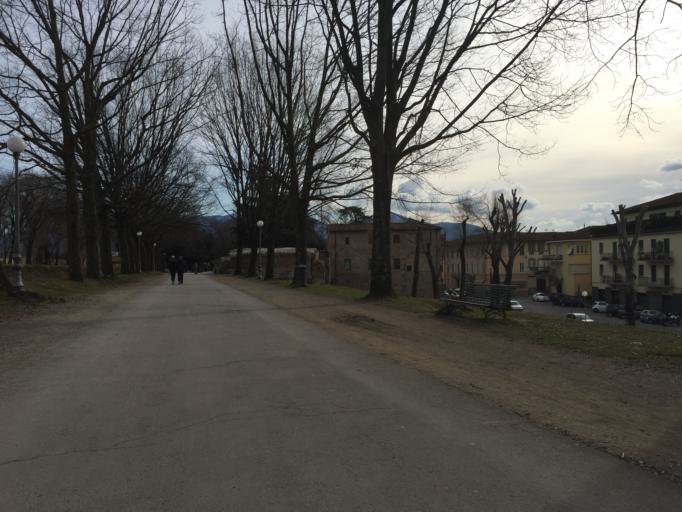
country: IT
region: Tuscany
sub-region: Provincia di Lucca
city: Lucca
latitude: 43.8467
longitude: 10.5143
